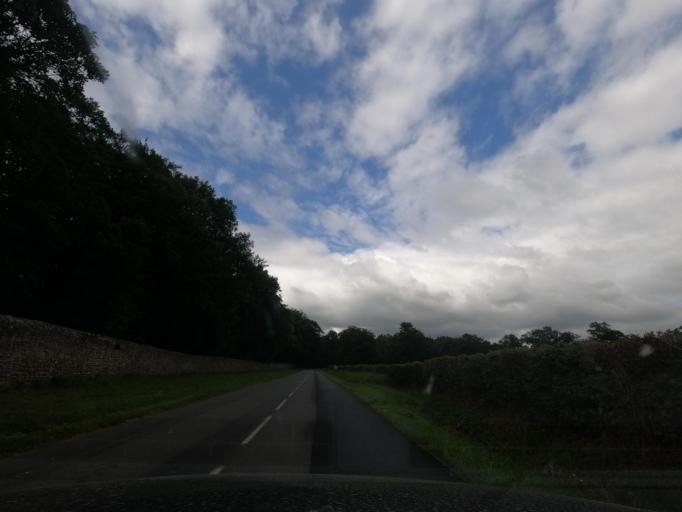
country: FR
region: Lower Normandy
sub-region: Departement de l'Orne
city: Briouze
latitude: 48.7241
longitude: -0.3479
